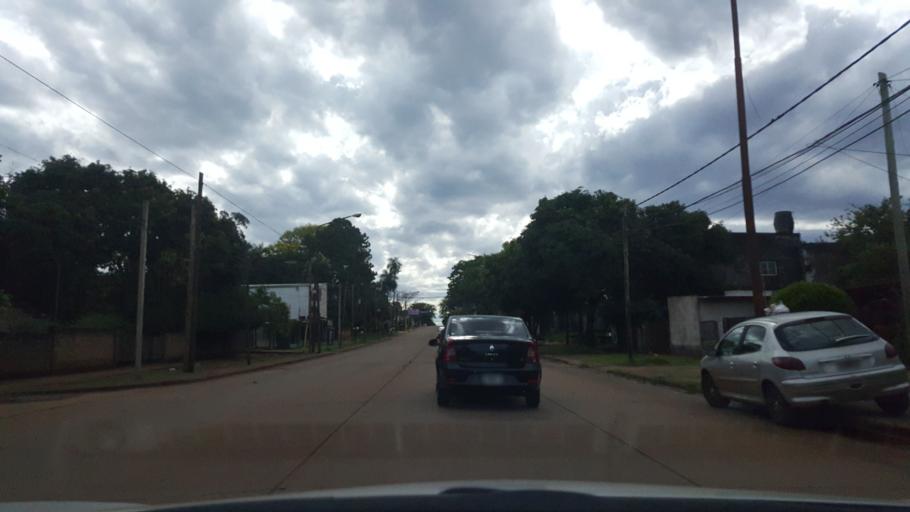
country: AR
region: Misiones
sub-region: Departamento de Capital
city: Posadas
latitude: -27.3721
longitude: -55.9181
